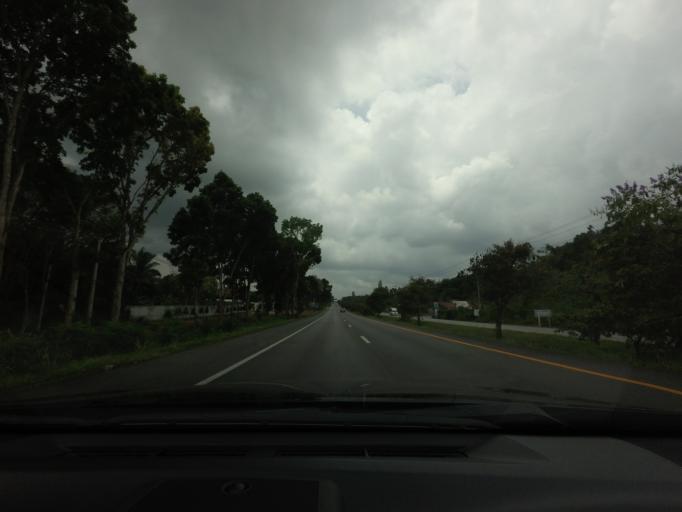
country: TH
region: Prachuap Khiri Khan
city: Bang Saphan Noi
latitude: 10.9662
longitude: 99.3197
